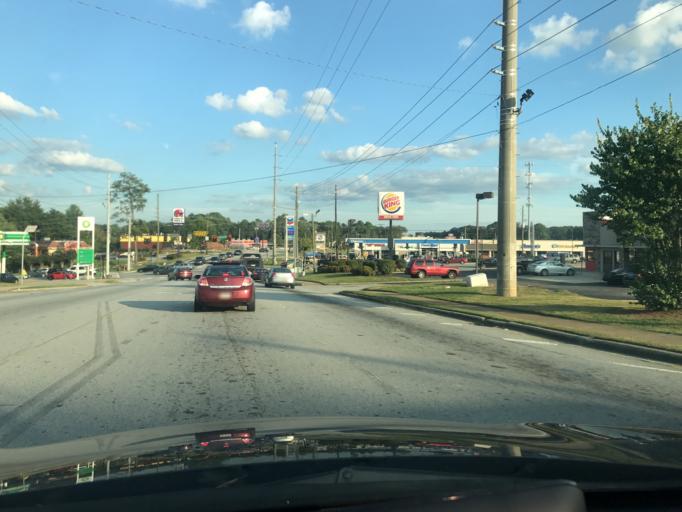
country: US
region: Georgia
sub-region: DeKalb County
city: Belvedere Park
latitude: 33.7555
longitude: -84.2688
